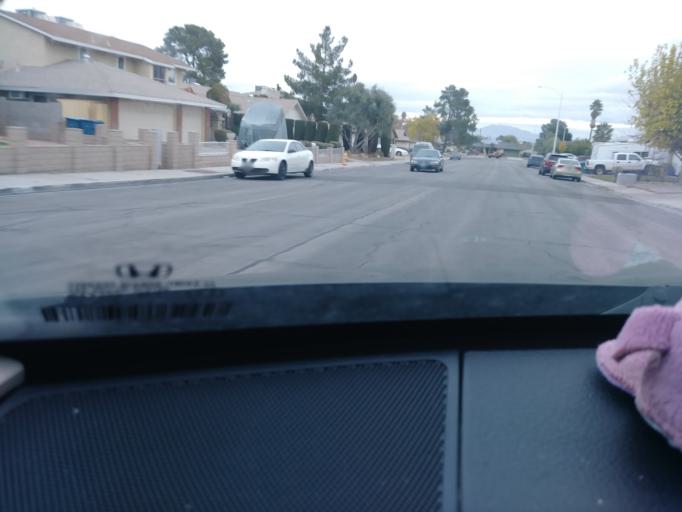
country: US
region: Nevada
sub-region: Clark County
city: Las Vegas
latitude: 36.1770
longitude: -115.2128
